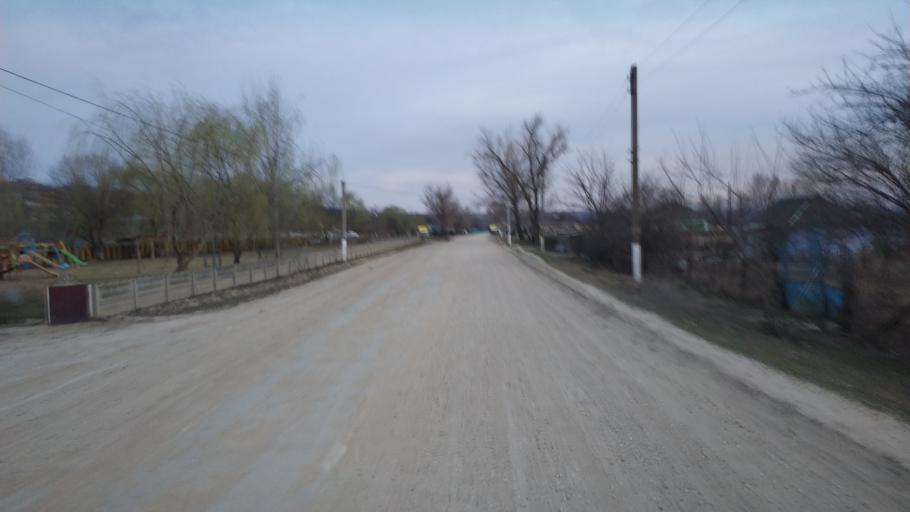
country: MD
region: Hincesti
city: Dancu
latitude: 46.7426
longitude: 28.2093
